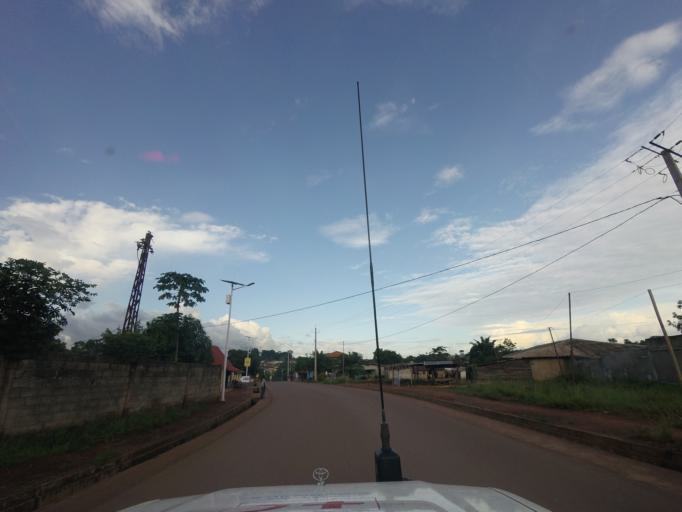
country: GN
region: Nzerekore
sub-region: Nzerekore Prefecture
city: Nzerekore
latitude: 7.7384
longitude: -8.8250
